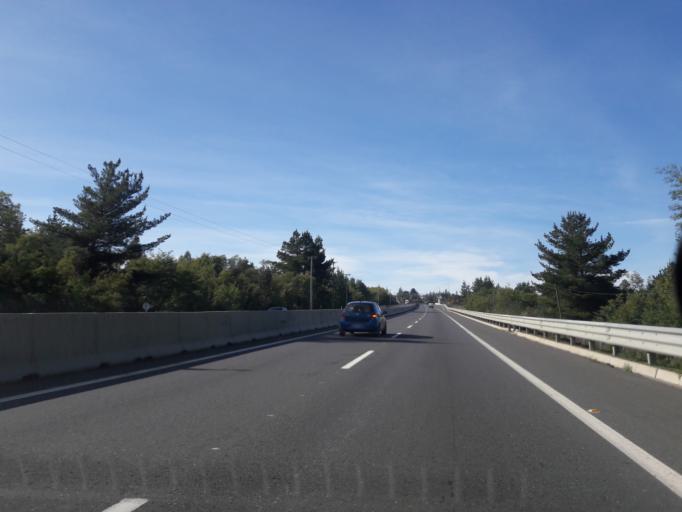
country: CL
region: Biobio
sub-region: Provincia de Biobio
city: Yumbel
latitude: -36.9746
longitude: -72.6609
